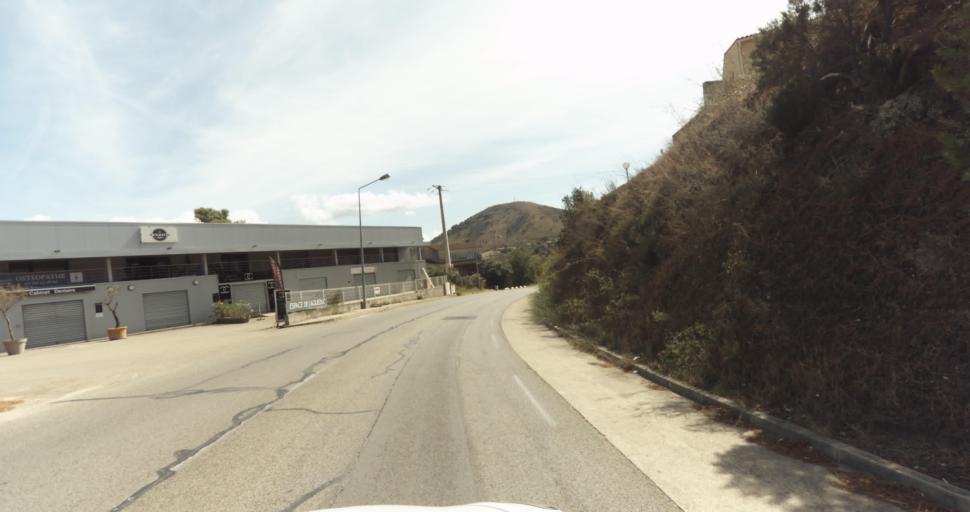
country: FR
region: Corsica
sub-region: Departement de la Corse-du-Sud
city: Afa
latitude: 41.9553
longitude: 8.7837
